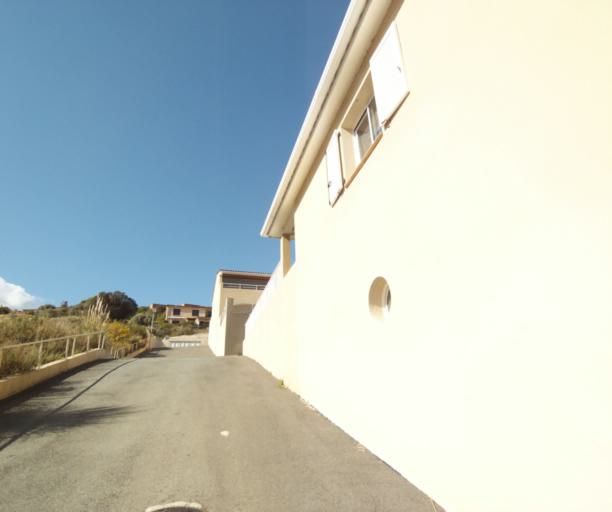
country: FR
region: Corsica
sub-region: Departement de la Corse-du-Sud
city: Propriano
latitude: 41.6719
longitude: 8.9006
